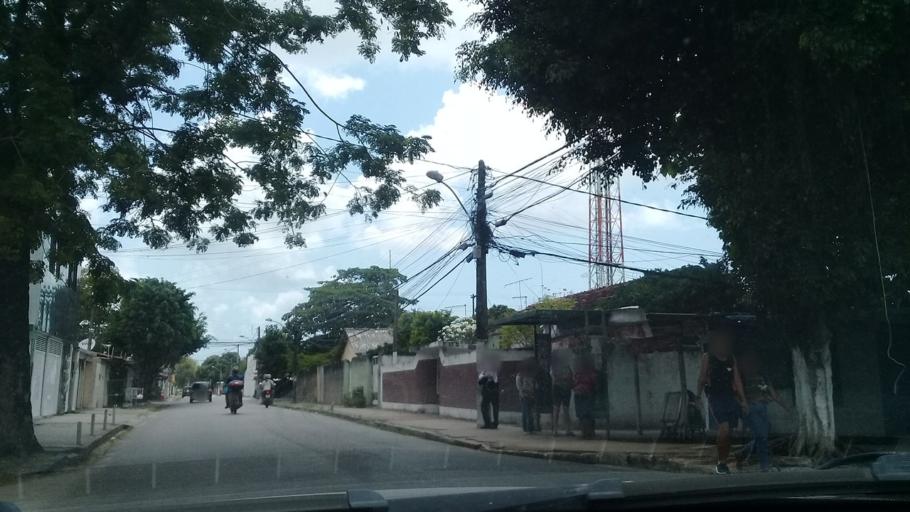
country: BR
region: Pernambuco
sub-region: Recife
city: Recife
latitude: -8.1077
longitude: -34.9252
